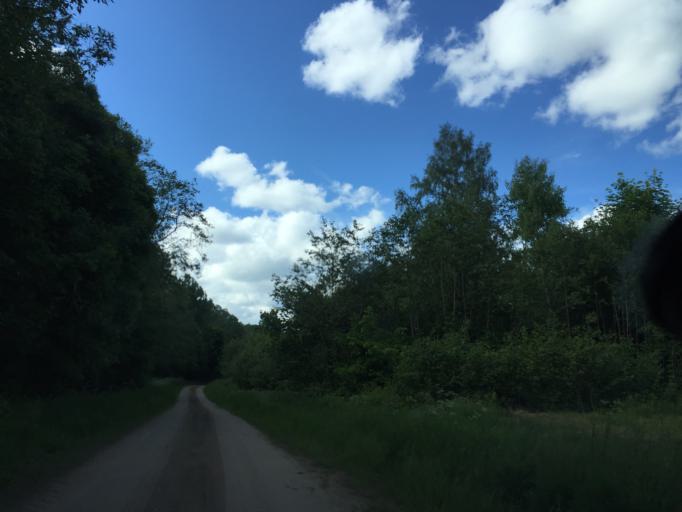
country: LV
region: Vecumnieki
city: Vecumnieki
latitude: 56.4244
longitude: 24.6147
